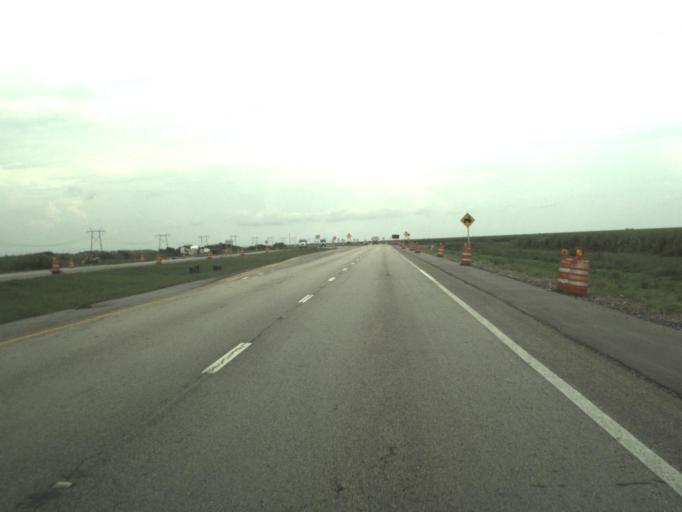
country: US
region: Florida
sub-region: Palm Beach County
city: Loxahatchee Groves
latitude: 26.7192
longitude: -80.4311
